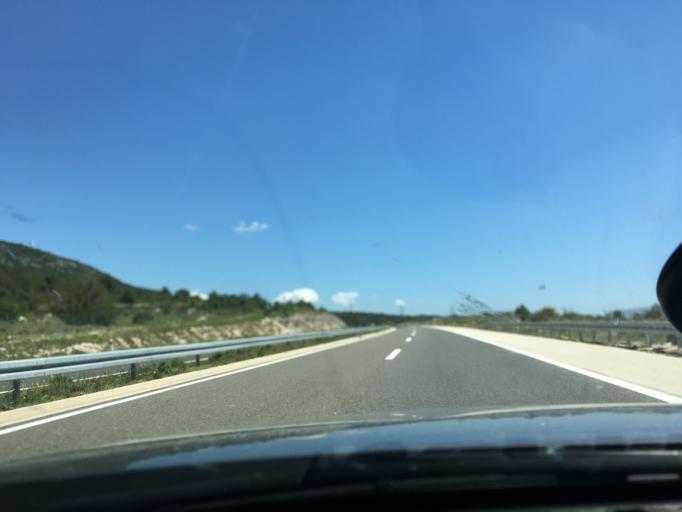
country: HR
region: Sibensko-Kniniska
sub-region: Grad Sibenik
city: Sibenik
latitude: 43.7469
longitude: 15.9573
